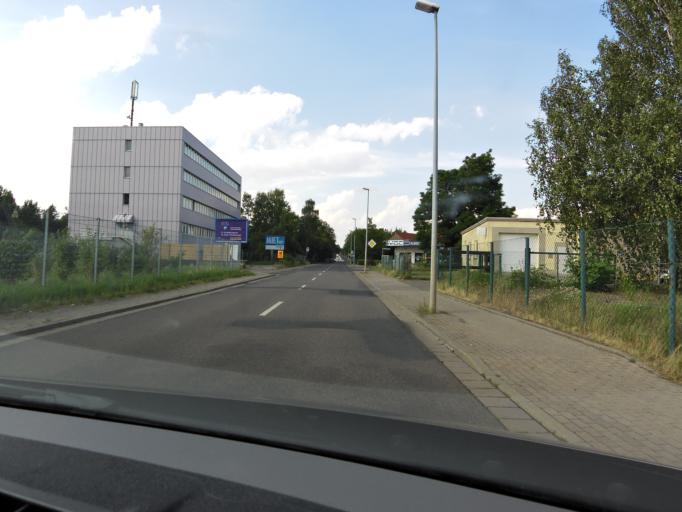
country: DE
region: Saxony
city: Grossposna
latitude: 51.3018
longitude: 12.4645
